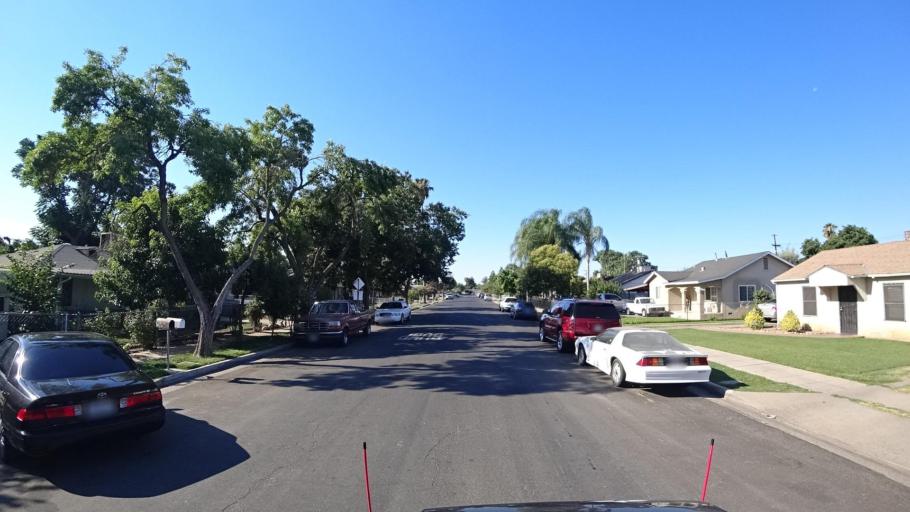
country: US
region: California
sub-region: Fresno County
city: Fresno
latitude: 36.7128
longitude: -119.7416
